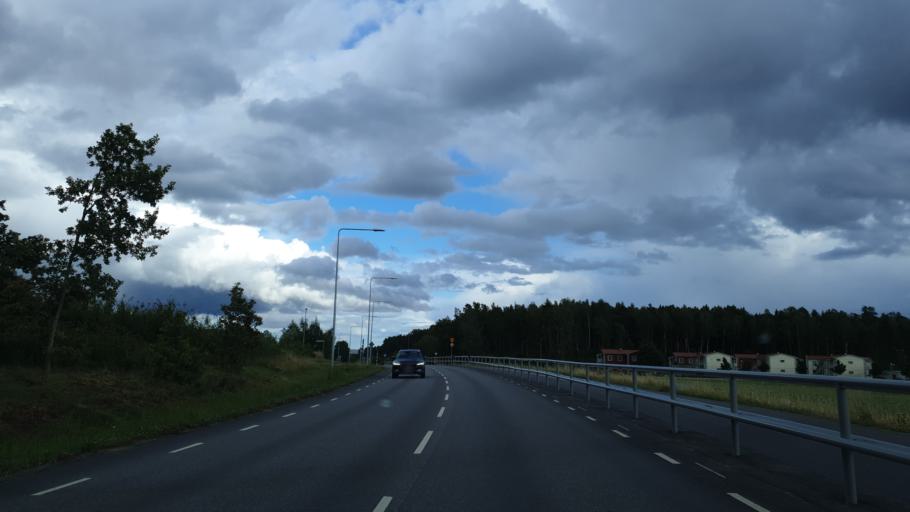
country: SE
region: Stockholm
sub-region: Jarfalla Kommun
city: Jakobsberg
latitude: 59.4243
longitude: 17.8014
